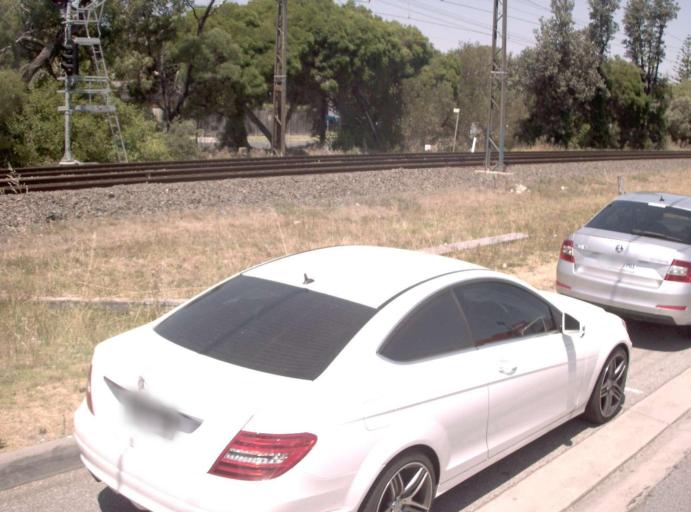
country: AU
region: Victoria
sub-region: Frankston
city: Frankston East
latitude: -38.1343
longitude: 145.1296
